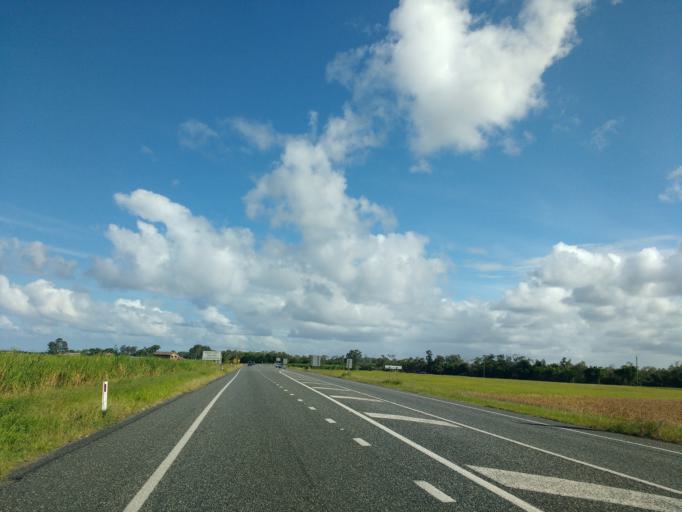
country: AU
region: New South Wales
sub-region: Ballina
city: Ballina
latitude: -28.9582
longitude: 153.4644
